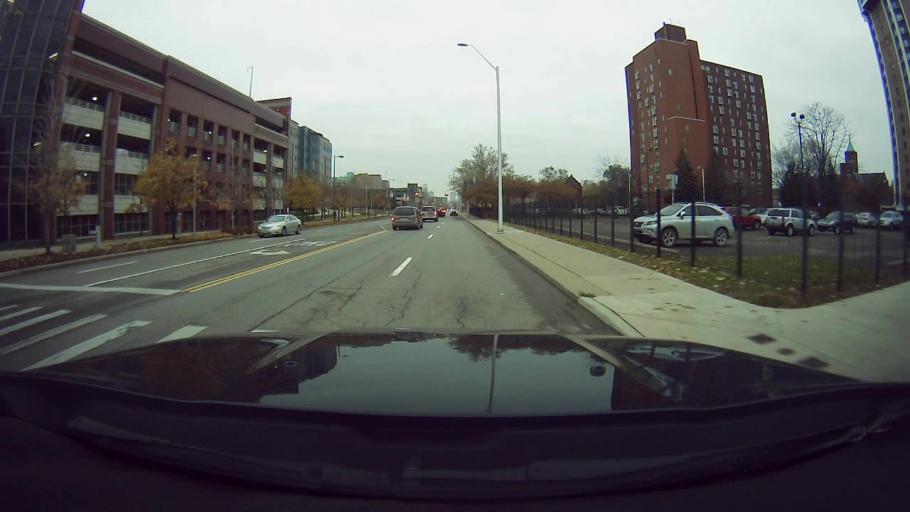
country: US
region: Michigan
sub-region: Wayne County
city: Detroit
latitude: 42.3567
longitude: -83.0615
